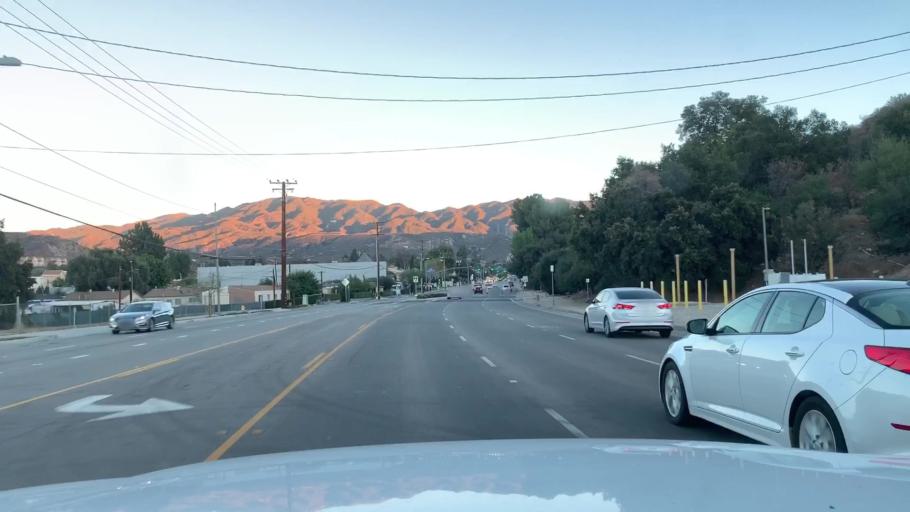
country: US
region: California
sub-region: Los Angeles County
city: Santa Clarita
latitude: 34.3733
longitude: -118.5191
